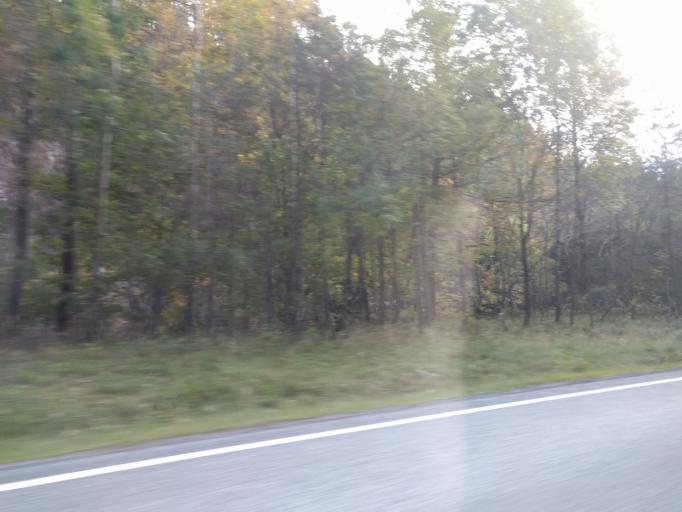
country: NO
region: Vest-Agder
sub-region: Kristiansand
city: Strai
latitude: 58.2444
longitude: 7.8774
